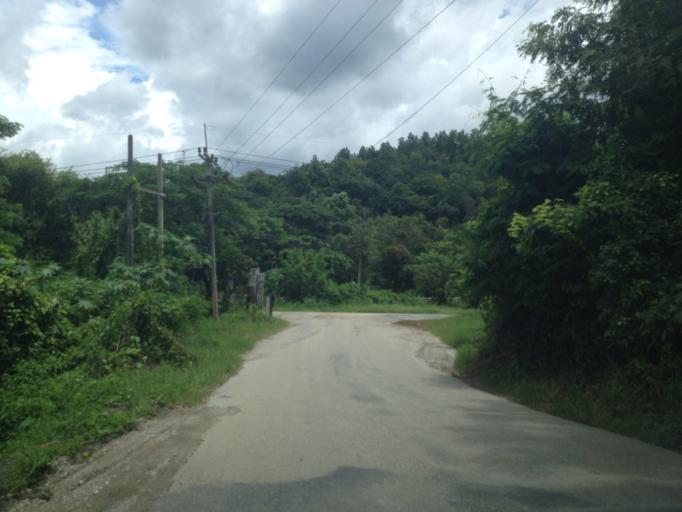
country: TH
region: Chiang Mai
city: Hang Dong
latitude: 18.7341
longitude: 98.8896
